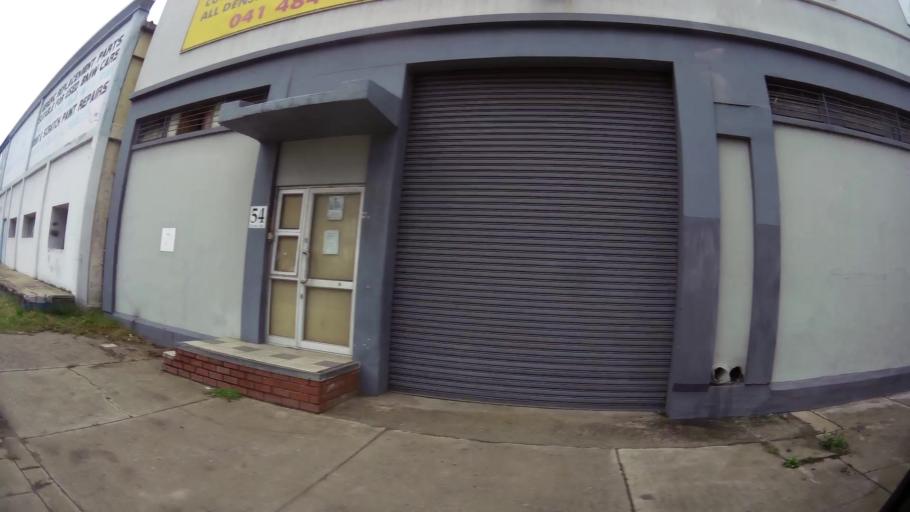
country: ZA
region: Eastern Cape
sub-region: Nelson Mandela Bay Metropolitan Municipality
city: Port Elizabeth
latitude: -33.9498
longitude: 25.6109
